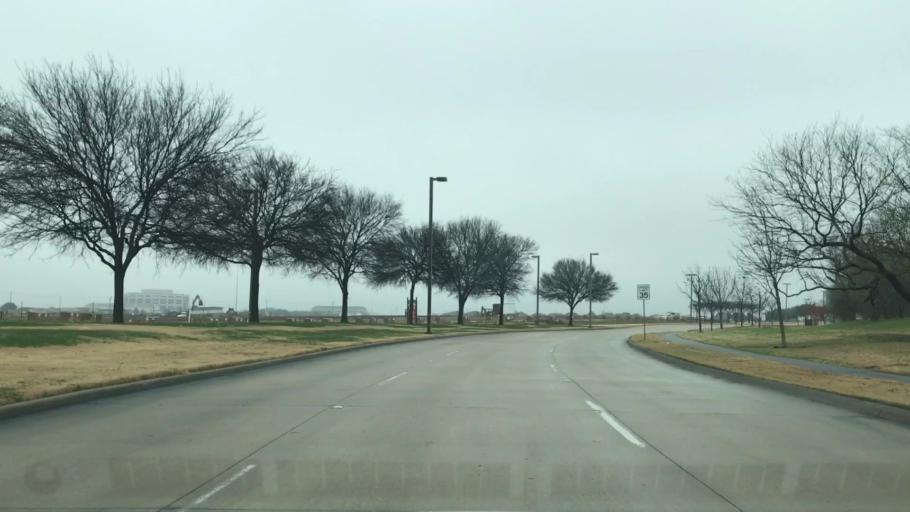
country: US
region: Texas
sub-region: Dallas County
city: Farmers Branch
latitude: 32.9012
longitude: -96.9536
